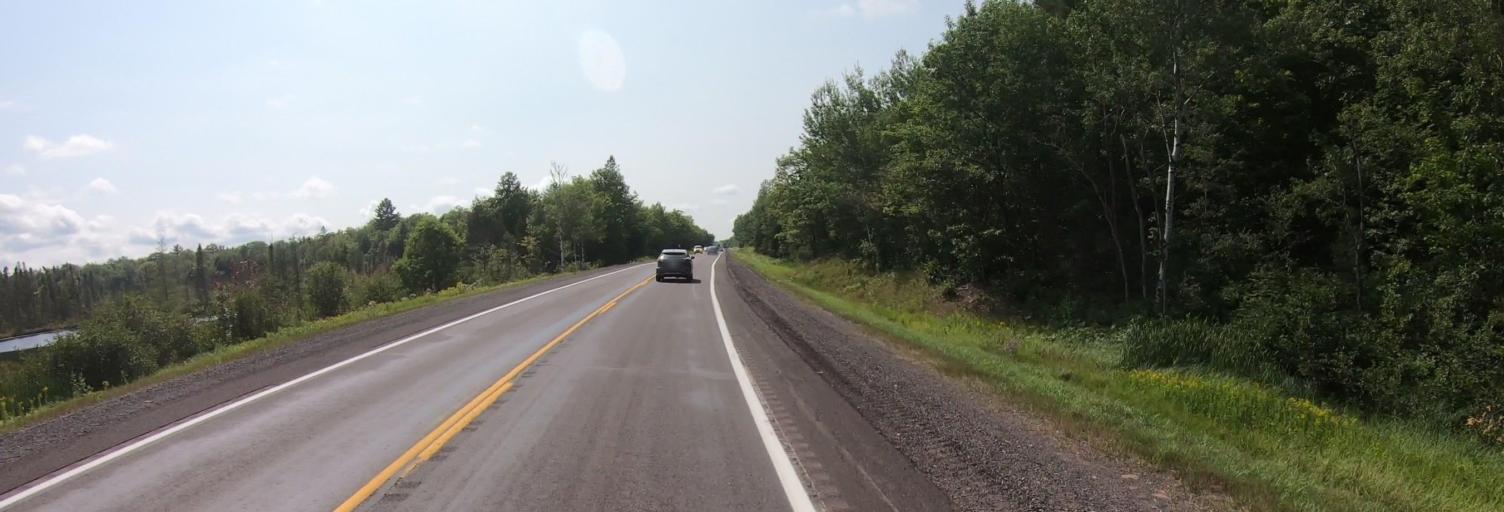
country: US
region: Michigan
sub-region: Houghton County
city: Hancock
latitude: 46.8710
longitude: -88.8792
